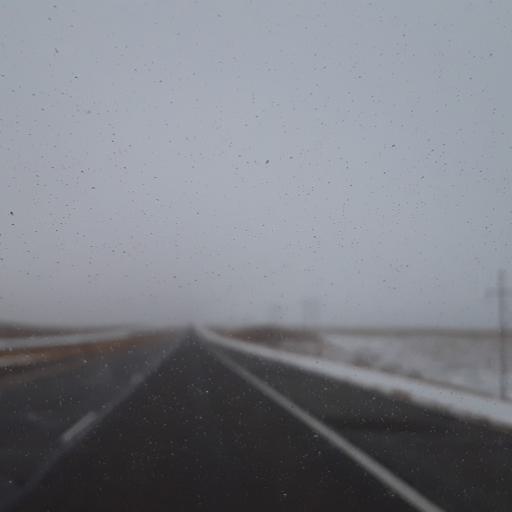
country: US
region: Nebraska
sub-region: Cheyenne County
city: Sidney
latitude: 40.8041
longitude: -102.8586
